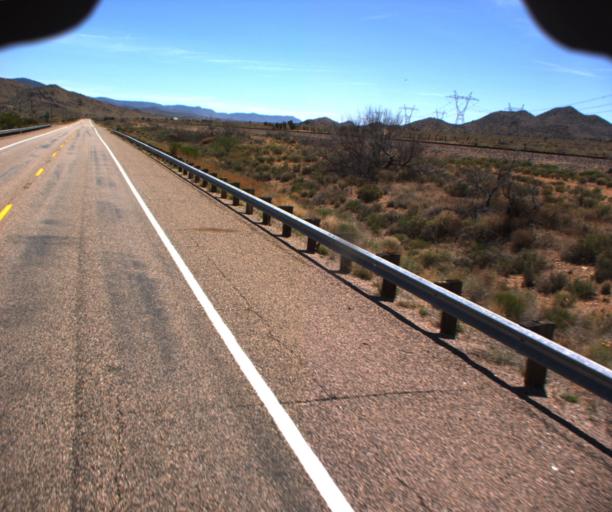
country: US
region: Arizona
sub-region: Mohave County
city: New Kingman-Butler
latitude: 35.3947
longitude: -113.7495
